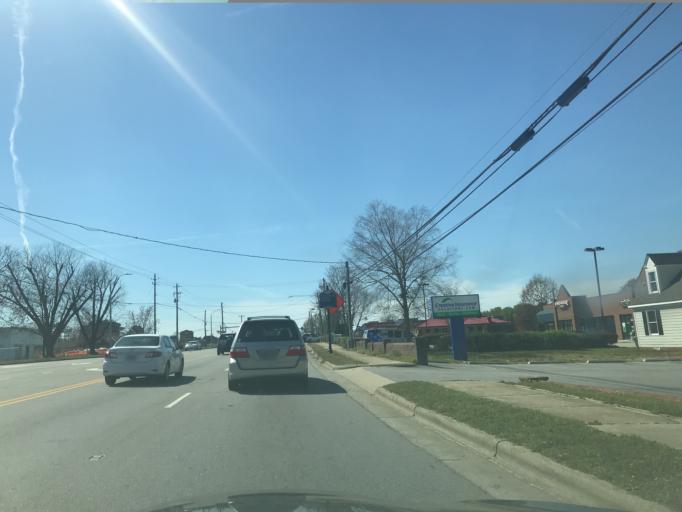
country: US
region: North Carolina
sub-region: Wake County
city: Fuquay-Varina
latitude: 35.5919
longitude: -78.7769
